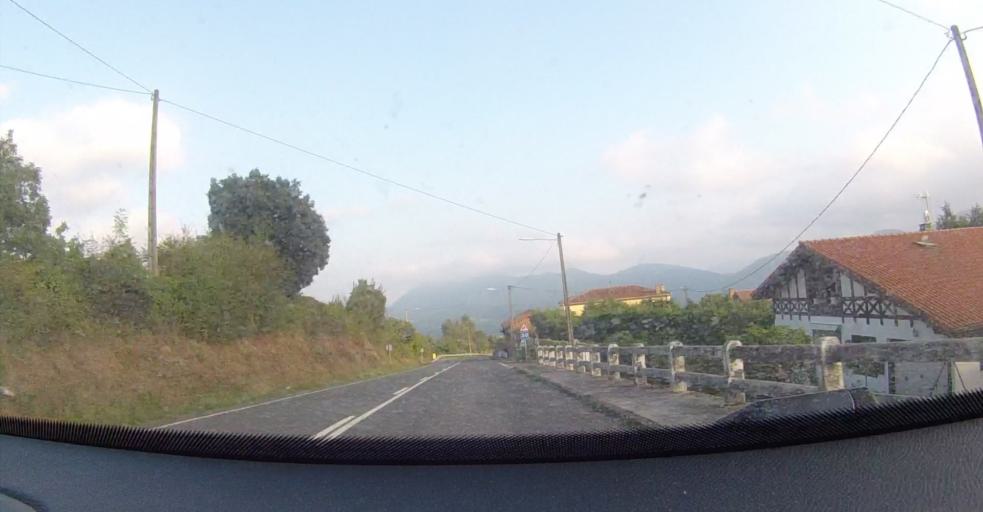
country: ES
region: Basque Country
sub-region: Bizkaia
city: Sopuerta
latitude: 43.2926
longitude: -3.1633
